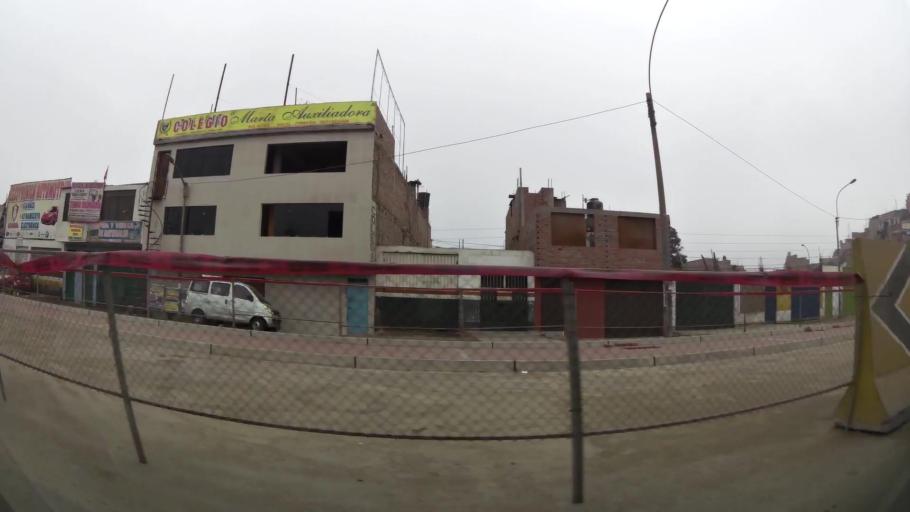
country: PE
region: Lima
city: Ventanilla
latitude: -11.8517
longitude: -77.0909
